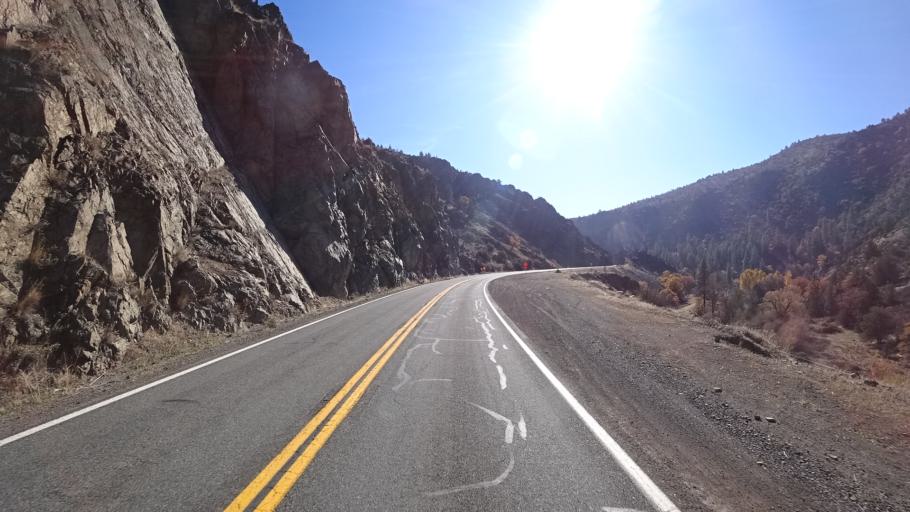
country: US
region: California
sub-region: Siskiyou County
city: Yreka
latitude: 41.8265
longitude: -122.5931
